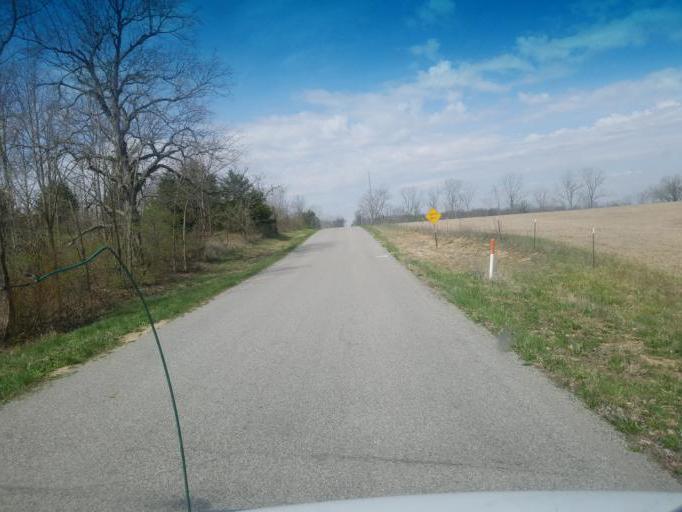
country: US
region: Ohio
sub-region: Logan County
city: Northwood
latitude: 40.4960
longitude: -83.6824
